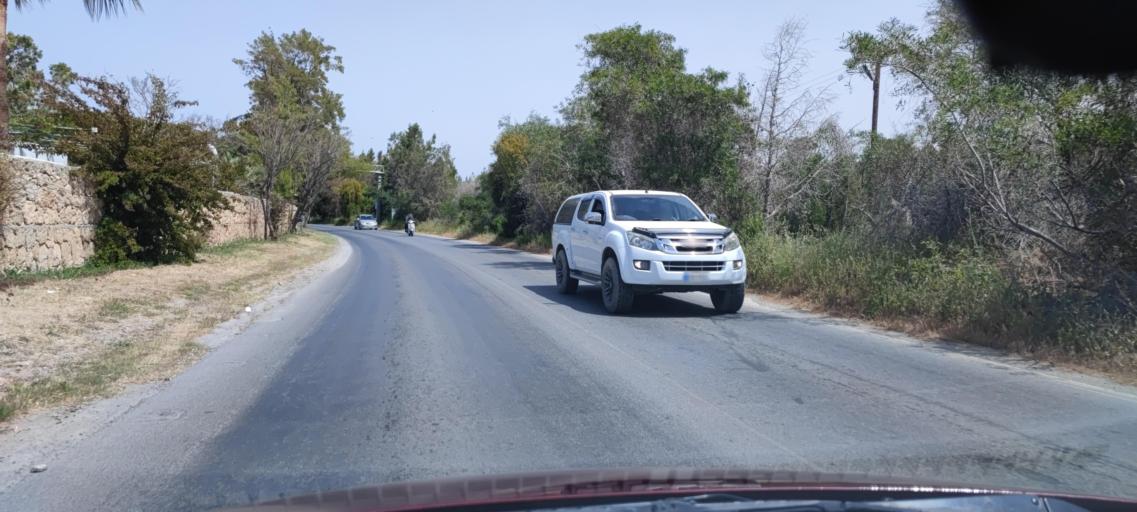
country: CY
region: Keryneia
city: Kyrenia
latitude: 35.3287
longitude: 33.4220
